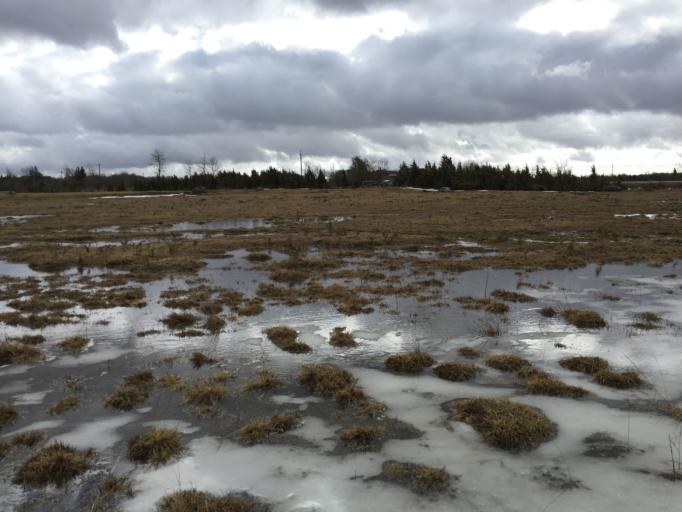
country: EE
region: Laeaene
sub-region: Ridala Parish
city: Uuemoisa
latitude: 58.7263
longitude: 23.5997
